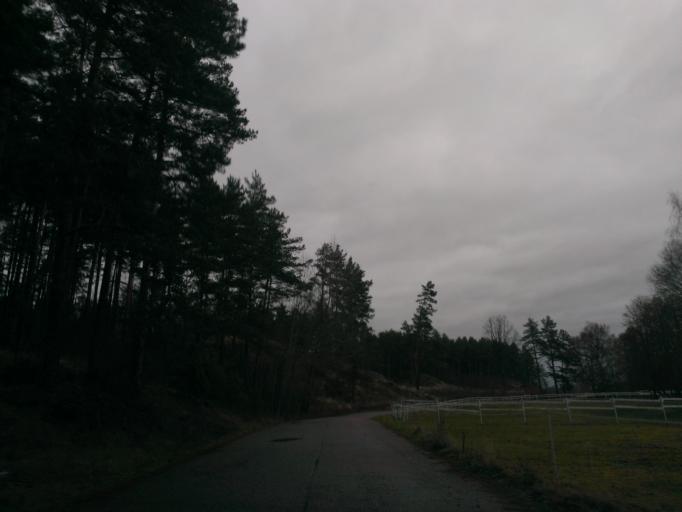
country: LV
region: Adazi
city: Adazi
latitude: 57.0597
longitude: 24.3546
